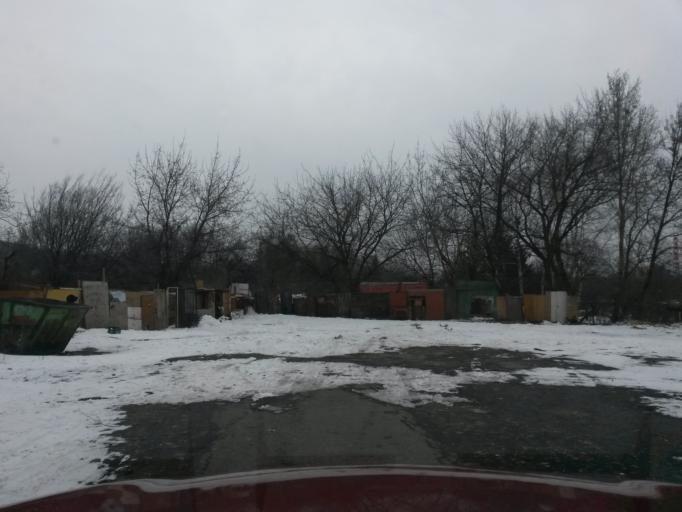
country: SK
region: Kosicky
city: Kosice
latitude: 48.7072
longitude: 21.2724
